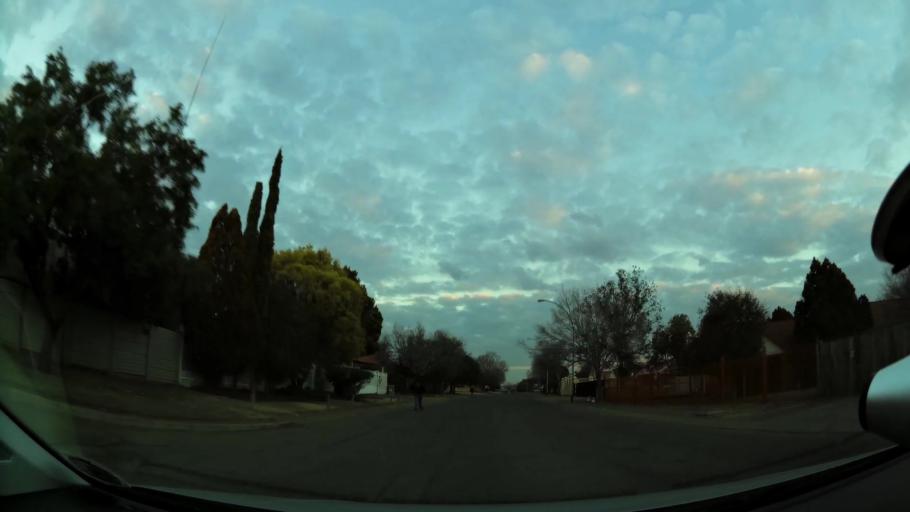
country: ZA
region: Orange Free State
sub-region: Mangaung Metropolitan Municipality
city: Bloemfontein
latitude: -29.1623
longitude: 26.1870
